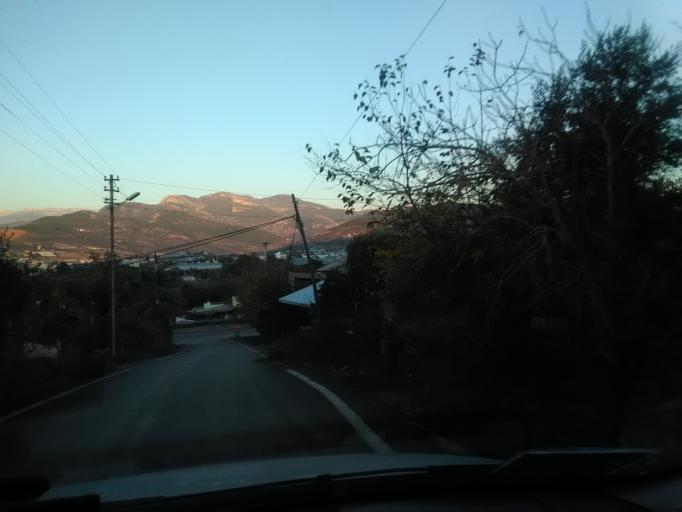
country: TR
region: Antalya
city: Gazipasa
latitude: 36.2481
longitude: 32.3408
